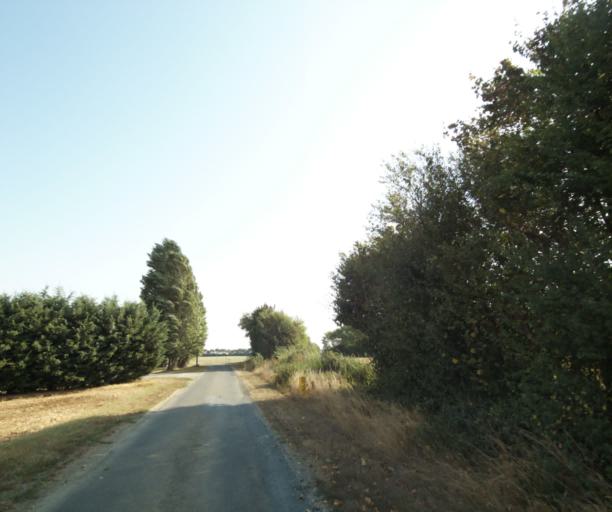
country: FR
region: Poitou-Charentes
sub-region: Departement de la Charente-Maritime
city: Cabariot
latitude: 45.9669
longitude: -0.8319
